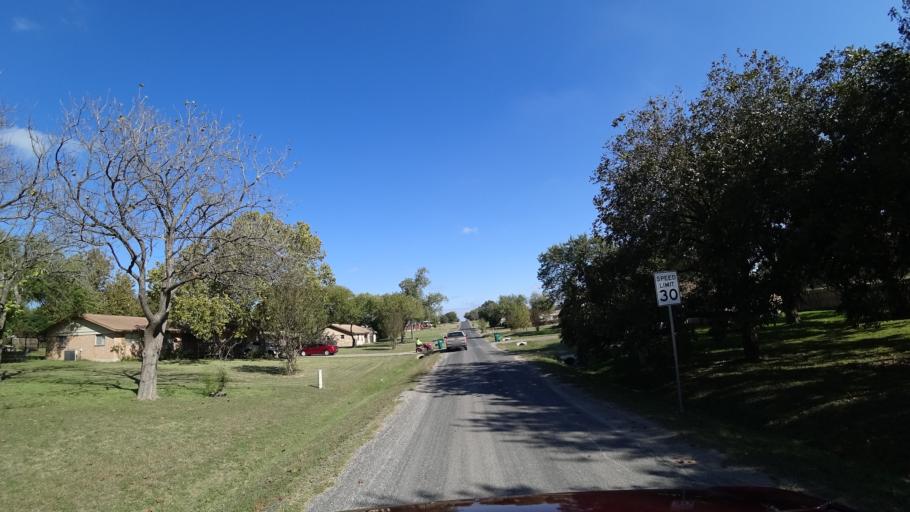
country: US
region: Texas
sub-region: Travis County
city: Windemere
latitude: 30.4390
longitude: -97.6504
